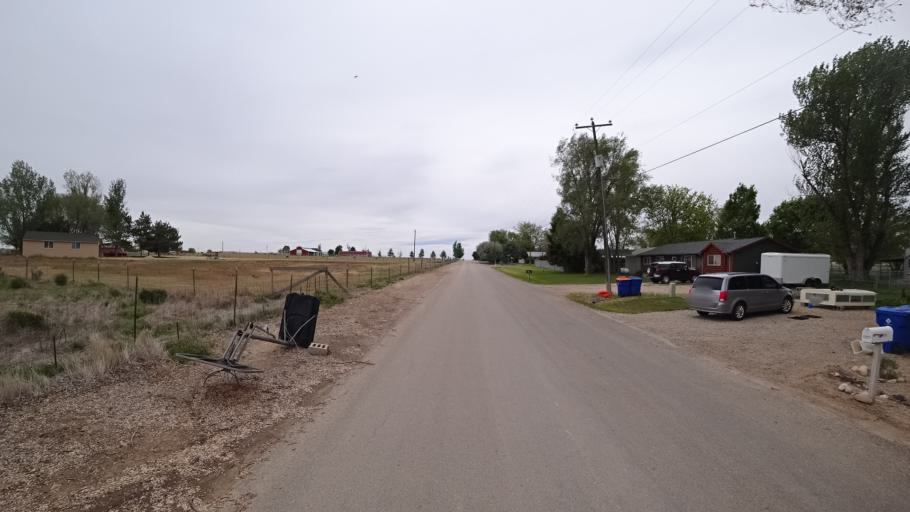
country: US
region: Idaho
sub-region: Ada County
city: Kuna
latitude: 43.4857
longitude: -116.3144
